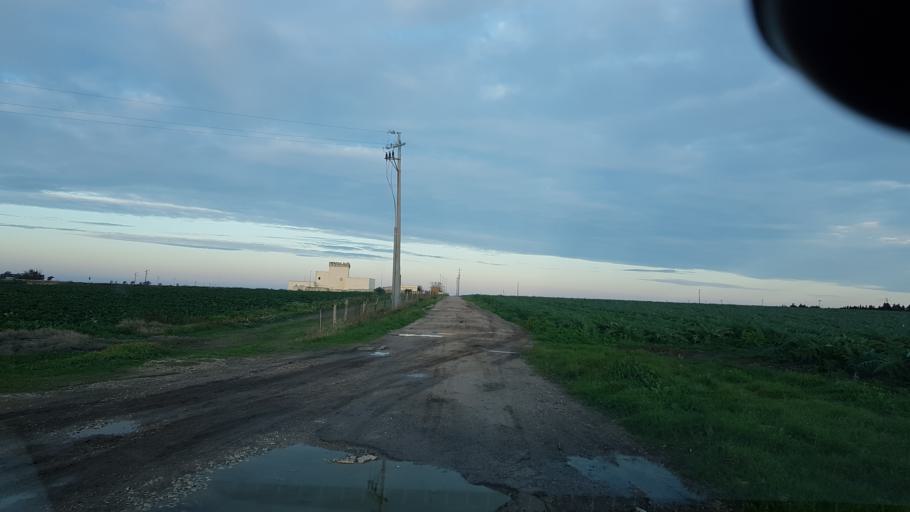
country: IT
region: Apulia
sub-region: Provincia di Brindisi
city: La Rosa
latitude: 40.6029
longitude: 18.0023
